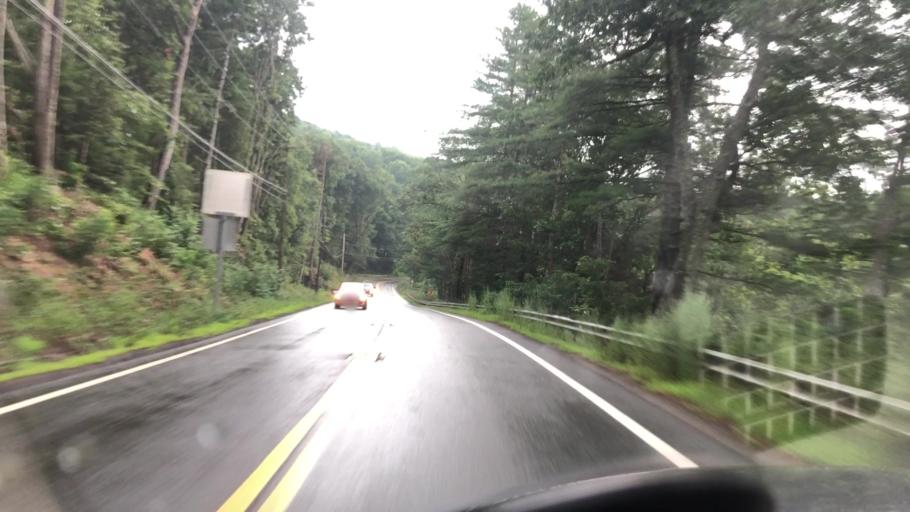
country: US
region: Massachusetts
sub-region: Hampshire County
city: Westhampton
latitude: 42.2760
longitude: -72.8633
